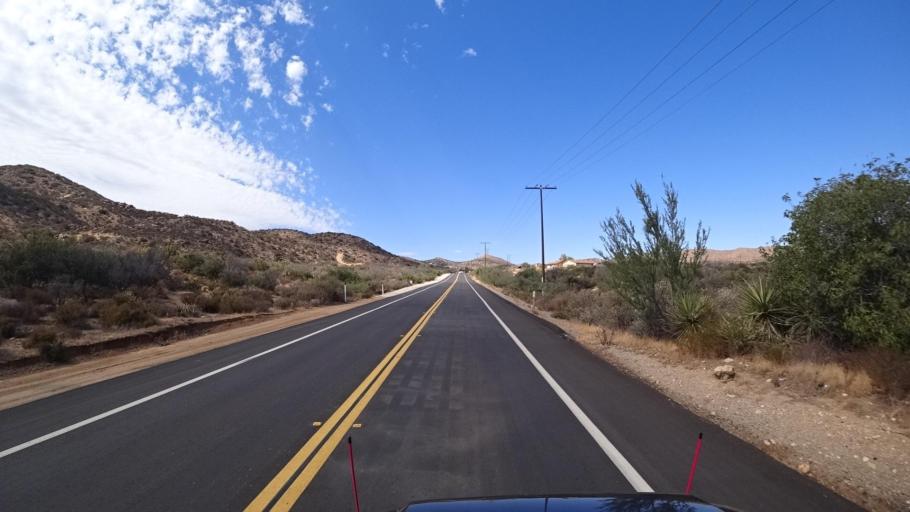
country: MX
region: Baja California
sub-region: Tecate
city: Cereso del Hongo
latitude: 32.6321
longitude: -116.2248
